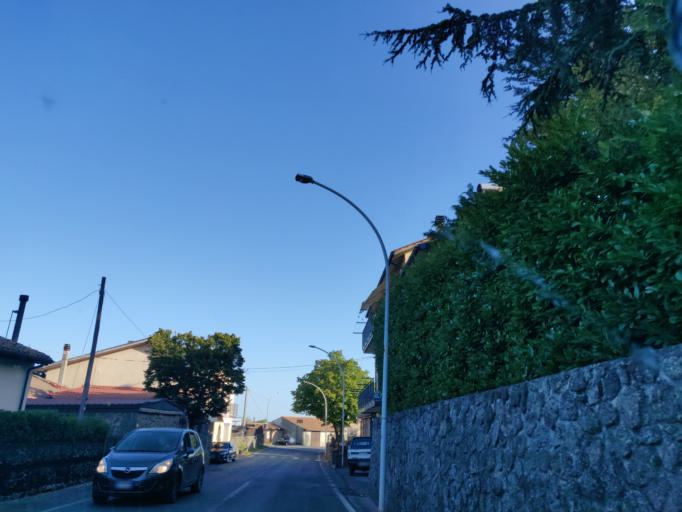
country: IT
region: Tuscany
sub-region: Provincia di Siena
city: Piancastagnaio
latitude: 42.8481
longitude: 11.6955
